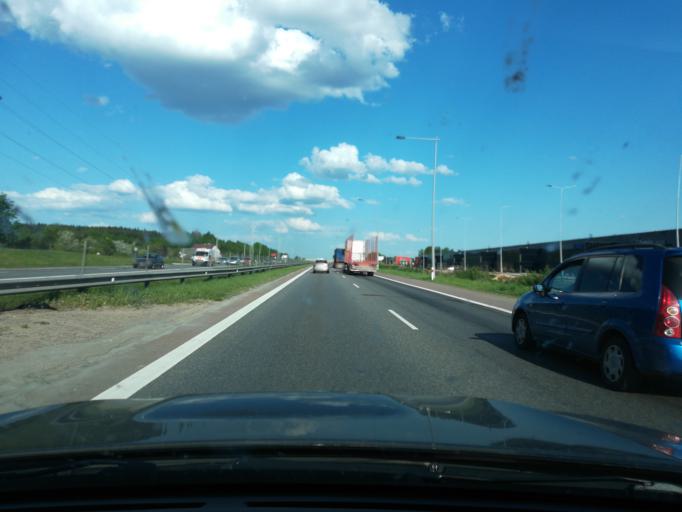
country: LT
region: Kauno apskritis
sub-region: Kaunas
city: Eiguliai
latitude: 54.9350
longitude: 23.9455
